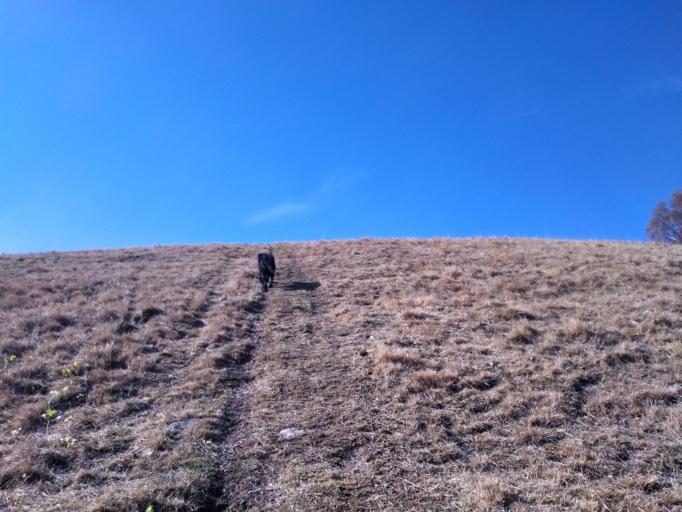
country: IT
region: Lombardy
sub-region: Provincia di Como
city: Rezzago
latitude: 45.8529
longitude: 9.2419
